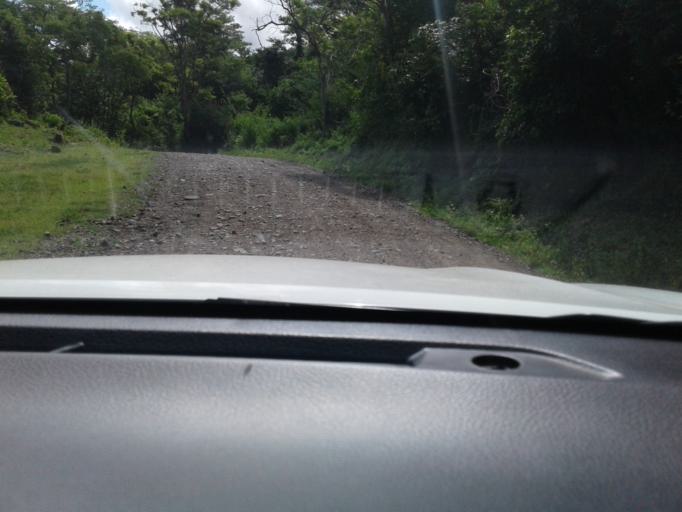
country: NI
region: Matagalpa
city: Ciudad Dario
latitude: 12.8426
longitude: -86.0554
